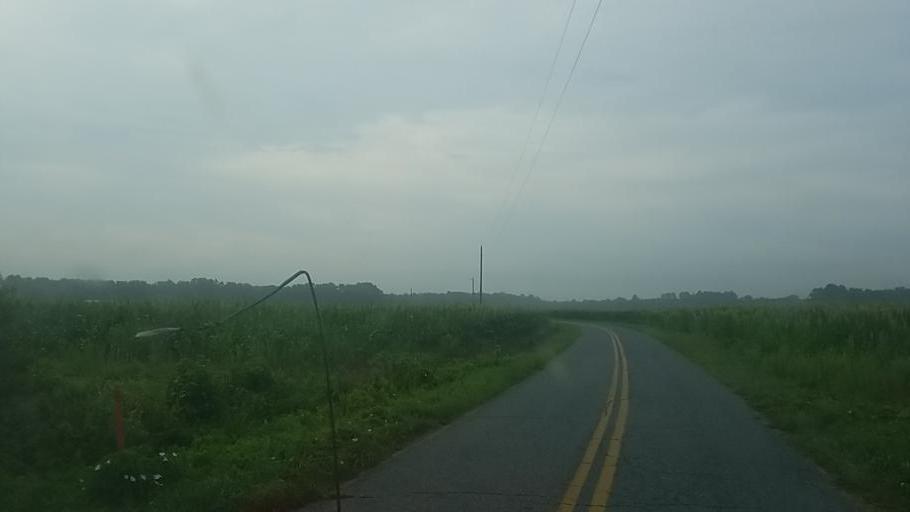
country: US
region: Maryland
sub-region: Wicomico County
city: Pittsville
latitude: 38.4357
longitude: -75.3282
